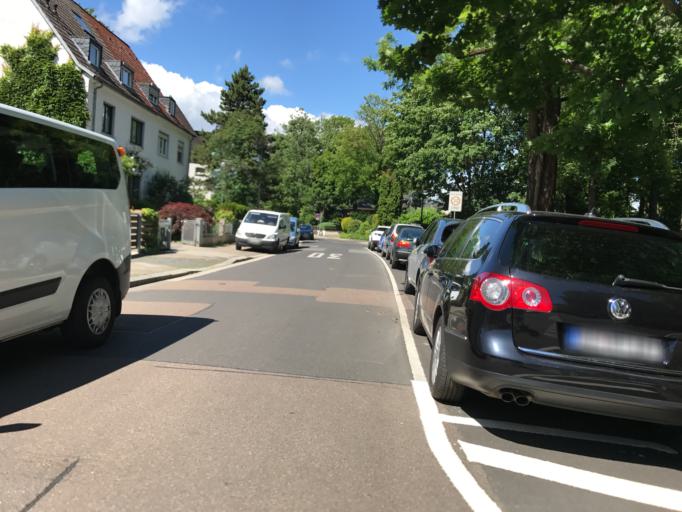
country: DE
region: Rheinland-Pfalz
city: Mainz
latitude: 49.9852
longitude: 8.2755
